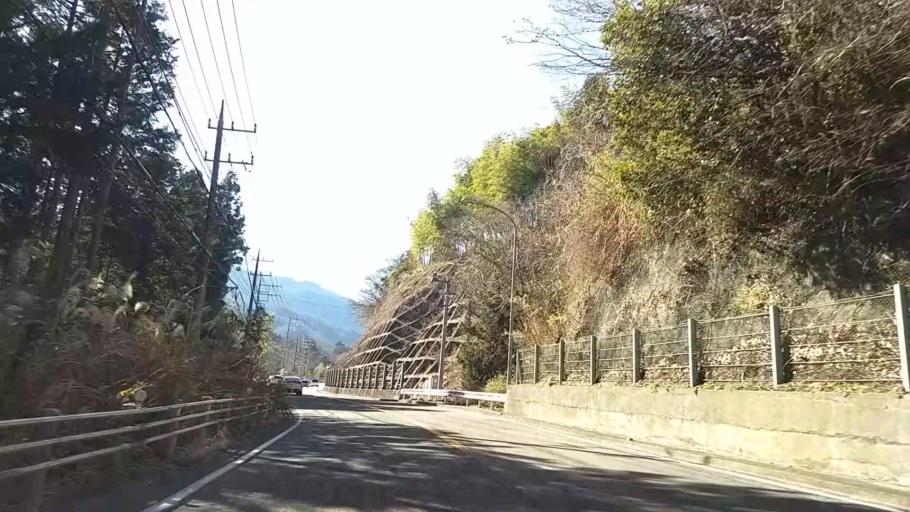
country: JP
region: Yamanashi
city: Uenohara
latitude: 35.6090
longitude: 139.0602
